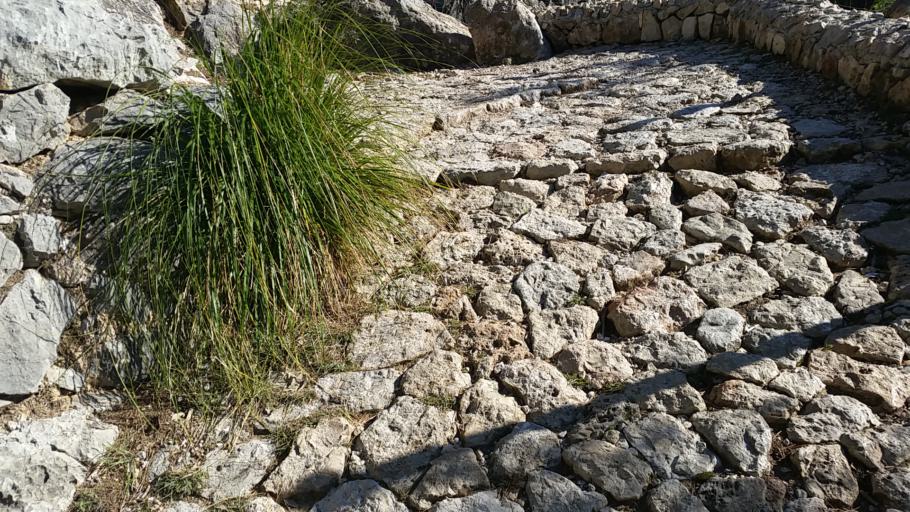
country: ES
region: Balearic Islands
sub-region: Illes Balears
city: Pollenca
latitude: 39.8676
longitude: 3.0200
